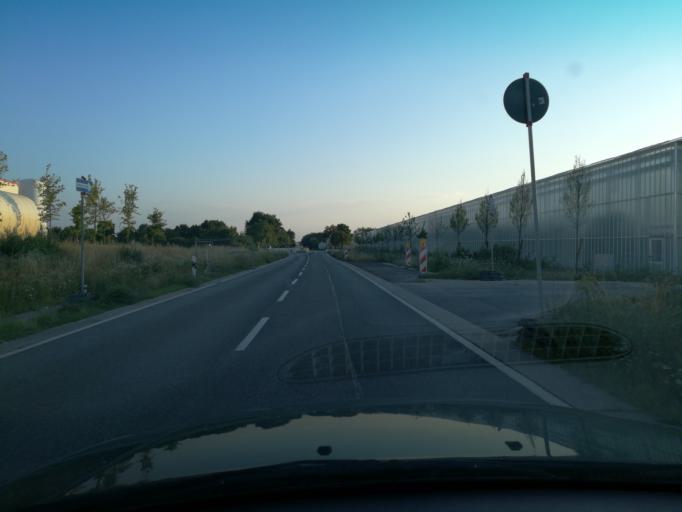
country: DE
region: Bavaria
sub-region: Regierungsbezirk Mittelfranken
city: Wetzendorf
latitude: 49.4804
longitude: 11.0362
